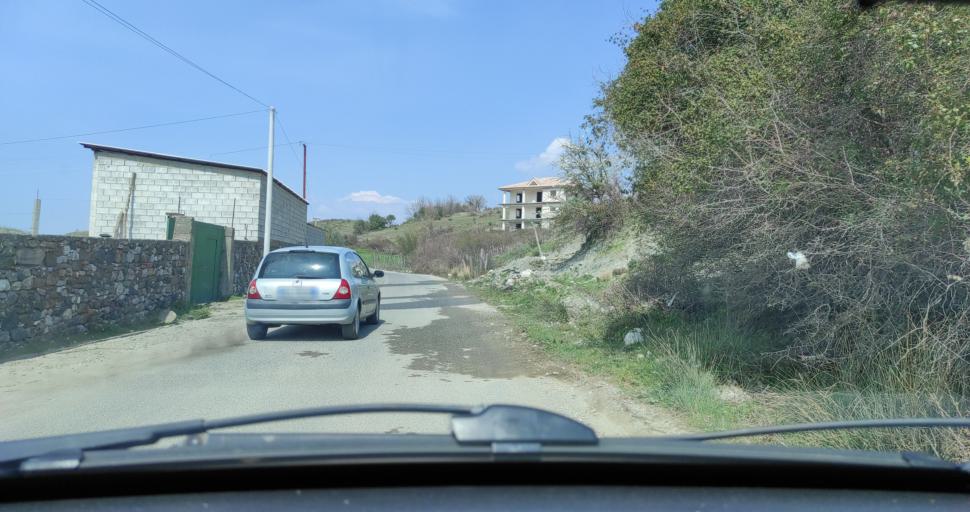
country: AL
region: Lezhe
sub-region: Rrethi i Lezhes
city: Kallmeti i Madh
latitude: 41.8616
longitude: 19.6989
